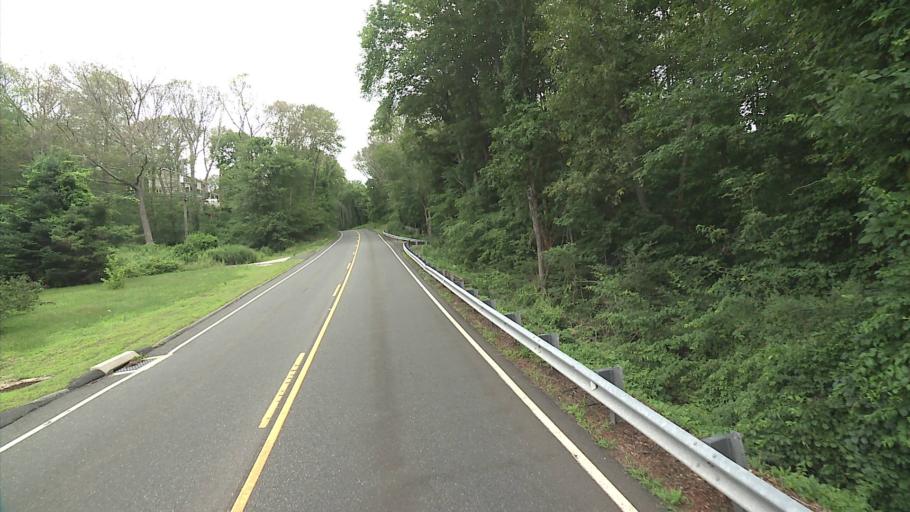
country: US
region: Connecticut
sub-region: New London County
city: Ledyard Center
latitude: 41.4631
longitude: -72.0191
